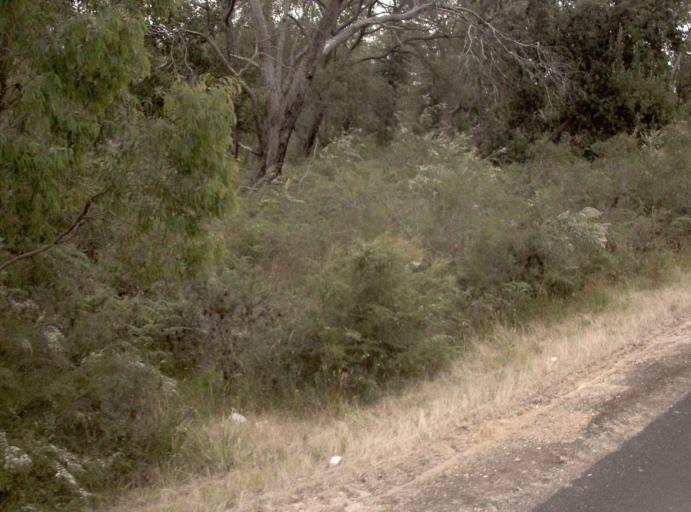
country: AU
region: Victoria
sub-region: Wellington
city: Sale
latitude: -38.2706
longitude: 147.0354
